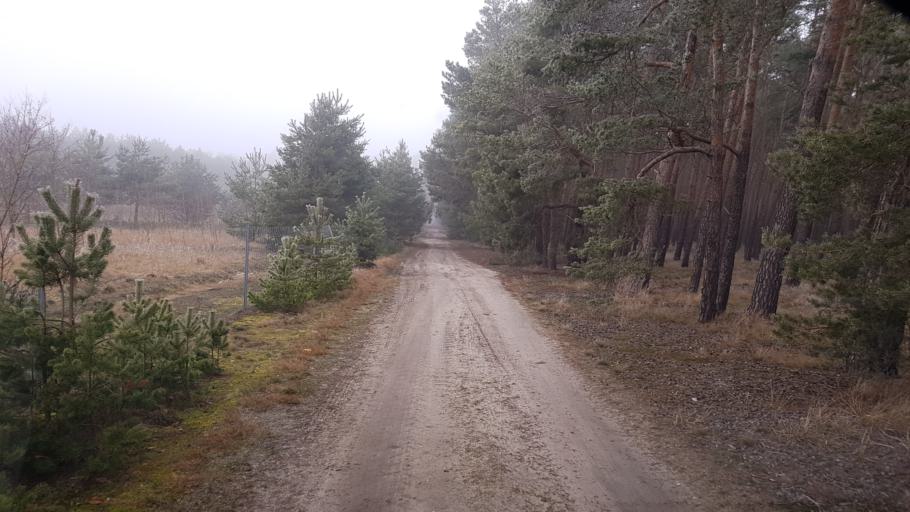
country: DE
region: Brandenburg
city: Ihlow
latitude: 51.8085
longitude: 13.2554
